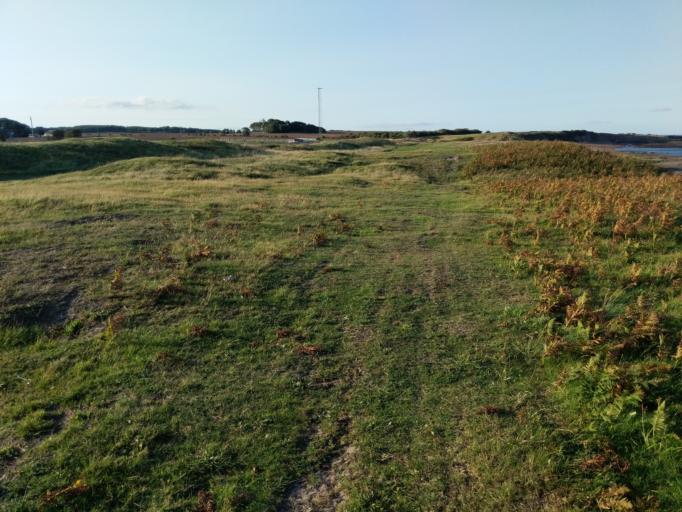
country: GB
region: England
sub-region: Northumberland
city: Lynemouth
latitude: 55.2175
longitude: -1.5289
